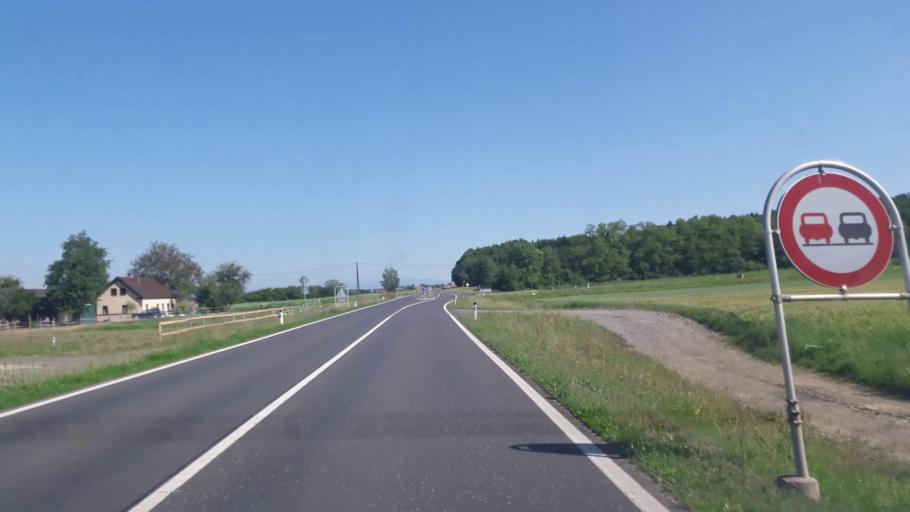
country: AT
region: Burgenland
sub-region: Politischer Bezirk Jennersdorf
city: Rudersdorf
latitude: 47.0665
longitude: 16.1141
